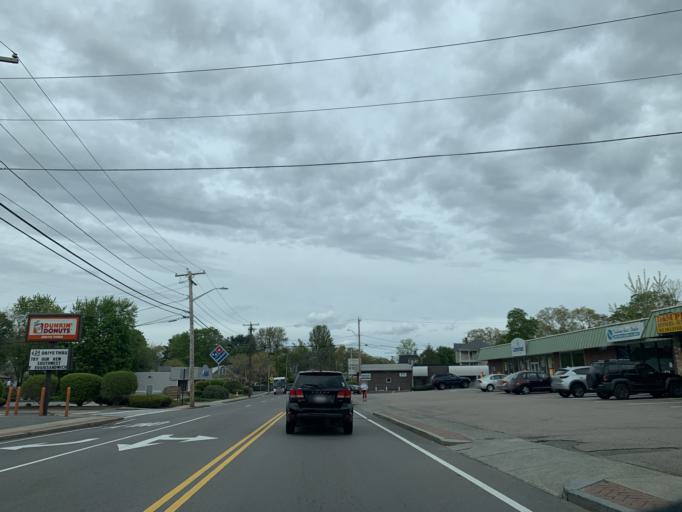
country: US
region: Massachusetts
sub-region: Bristol County
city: Attleboro
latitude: 41.9339
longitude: -71.2999
